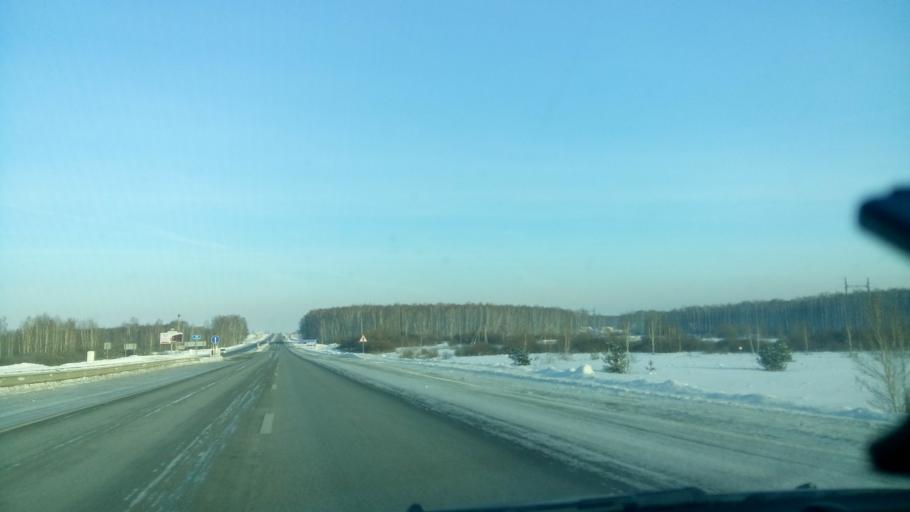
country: RU
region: Chelyabinsk
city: Dolgoderevenskoye
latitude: 55.3692
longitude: 61.3250
